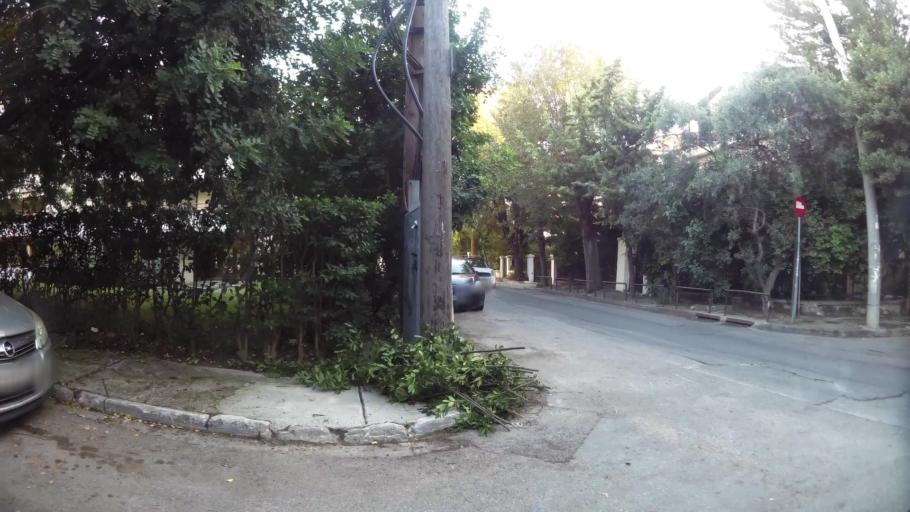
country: GR
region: Attica
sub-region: Nomarchia Athinas
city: Kifisia
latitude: 38.0719
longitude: 23.8055
